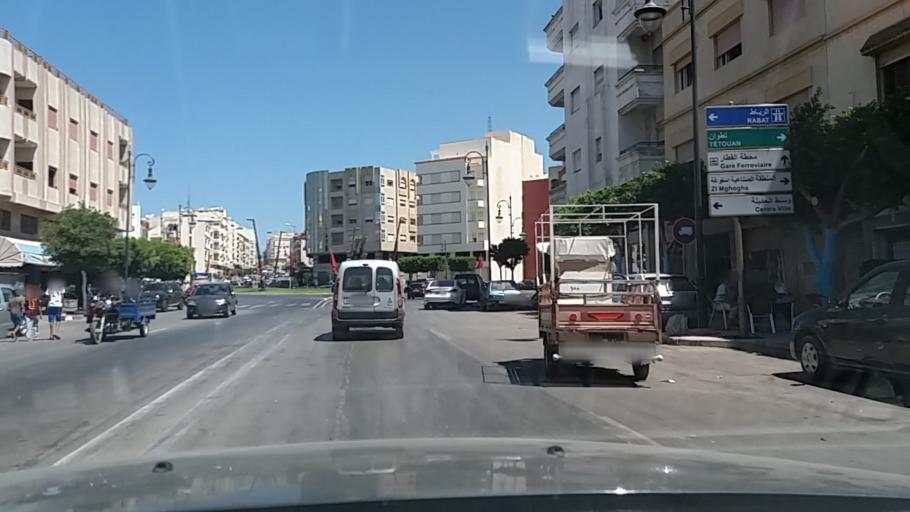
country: MA
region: Tanger-Tetouan
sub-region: Tanger-Assilah
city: Tangier
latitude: 35.7610
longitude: -5.7956
